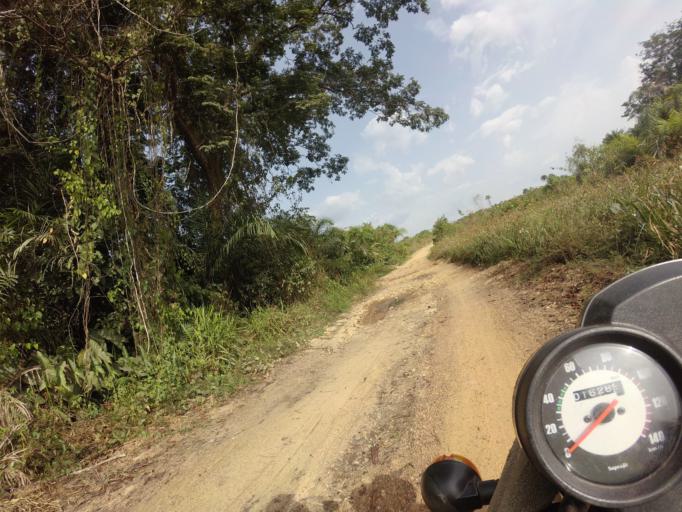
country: SL
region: Southern Province
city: Zimmi
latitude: 7.2250
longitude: -11.1901
